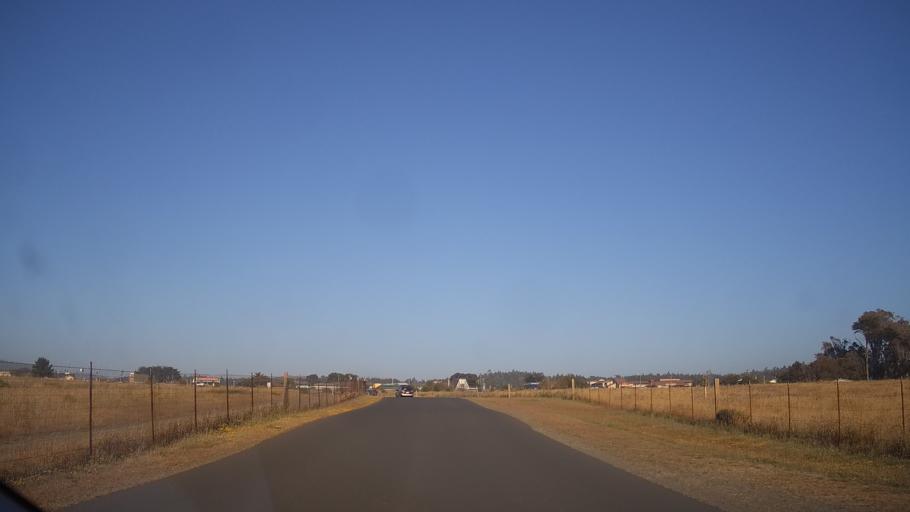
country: US
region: California
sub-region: Mendocino County
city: Fort Bragg
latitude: 39.4324
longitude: -123.8108
